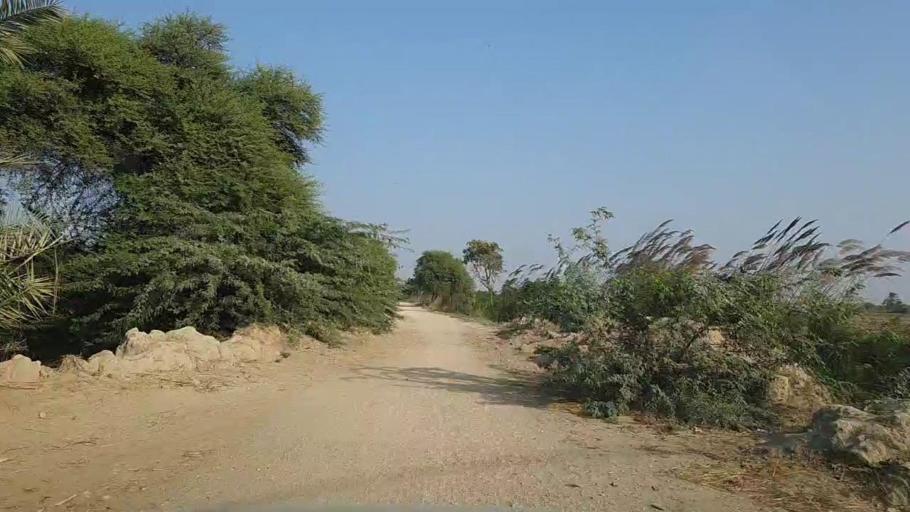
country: PK
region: Sindh
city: Mirpur Sakro
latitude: 24.5999
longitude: 67.6507
